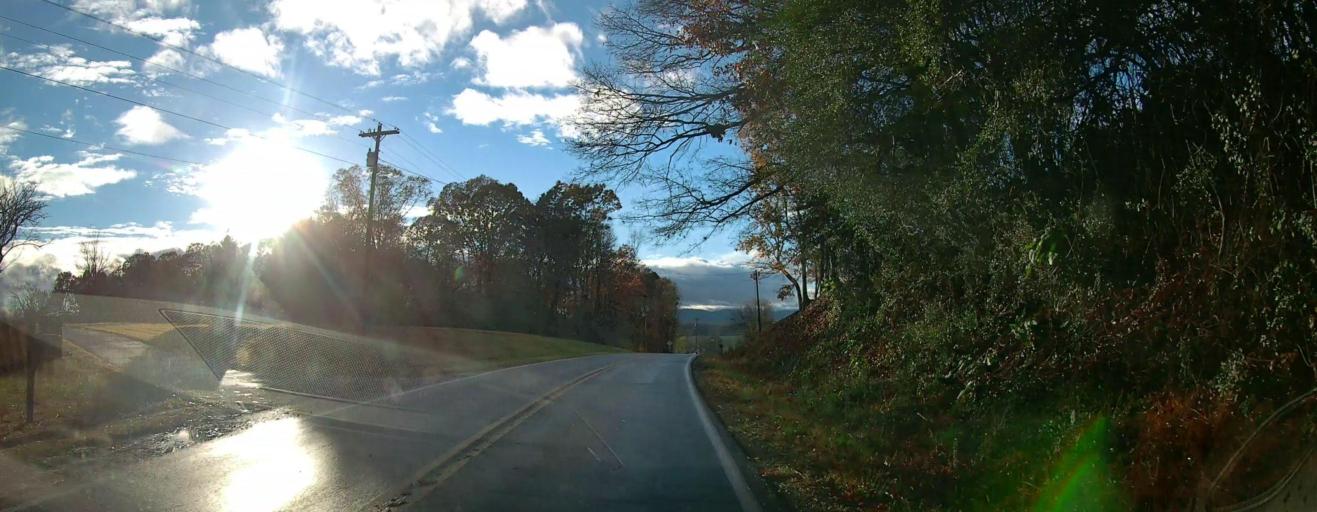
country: US
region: Georgia
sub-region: White County
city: Cleveland
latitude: 34.5441
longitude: -83.6931
